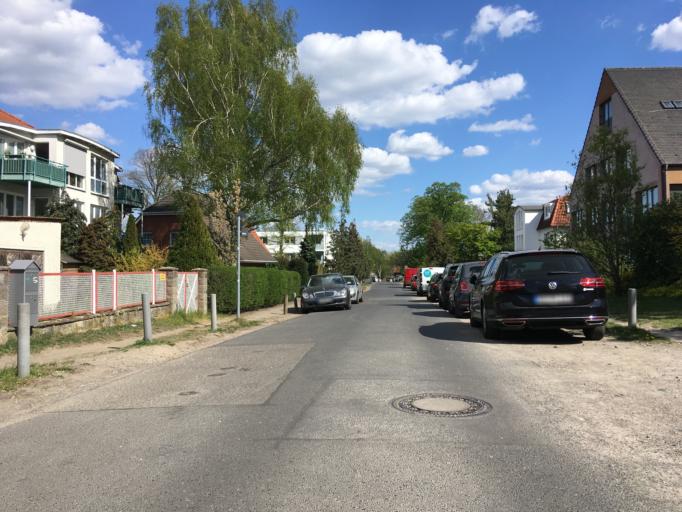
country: DE
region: Berlin
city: Mahlsdorf
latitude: 52.5092
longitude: 13.6193
